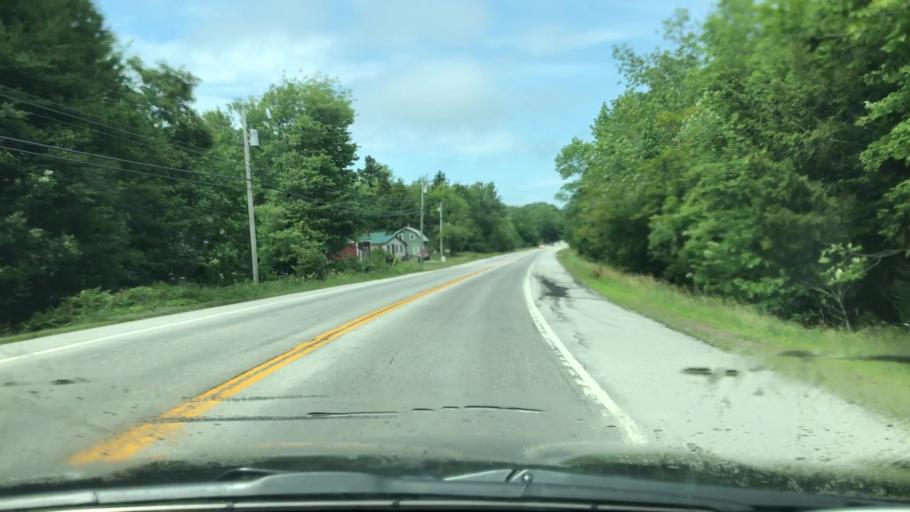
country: US
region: Maine
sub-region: Waldo County
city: Northport
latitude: 44.3450
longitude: -68.9697
